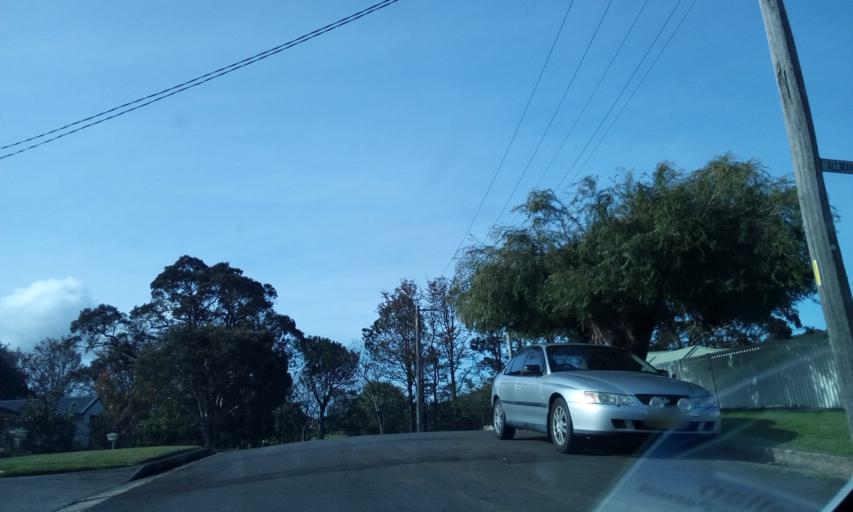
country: AU
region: New South Wales
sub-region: Wollongong
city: Mount Saint Thomas
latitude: -34.4419
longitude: 150.8688
